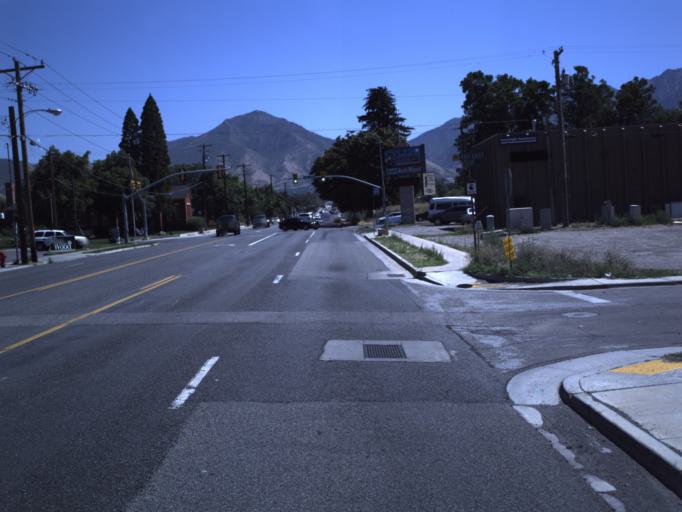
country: US
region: Utah
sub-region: Salt Lake County
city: Millcreek
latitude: 40.6998
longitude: -111.8781
